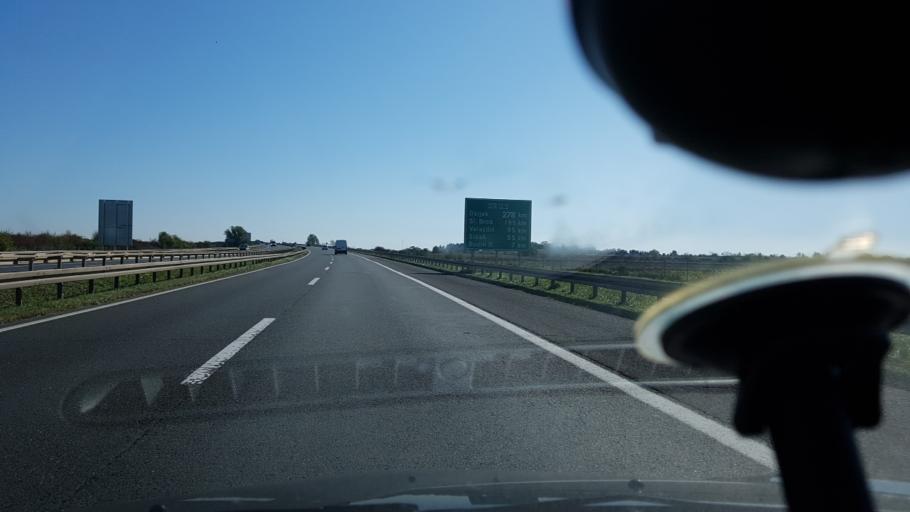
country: HR
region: Grad Zagreb
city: Zadvorsko
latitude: 45.7516
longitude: 15.9101
